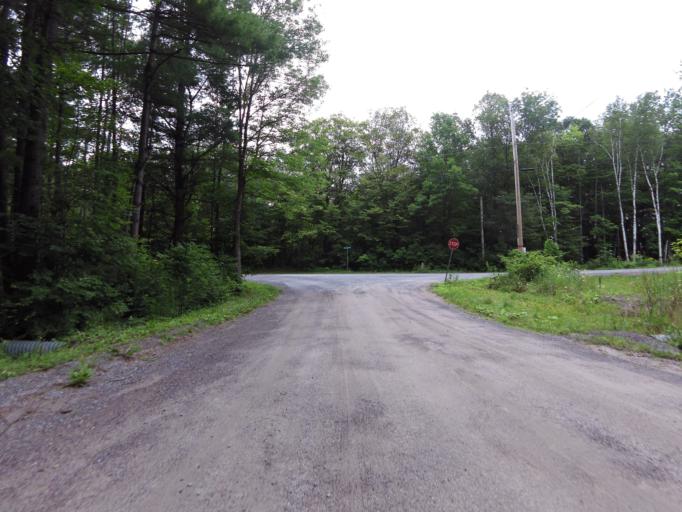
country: CA
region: Ontario
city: Kingston
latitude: 44.5688
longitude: -76.5484
